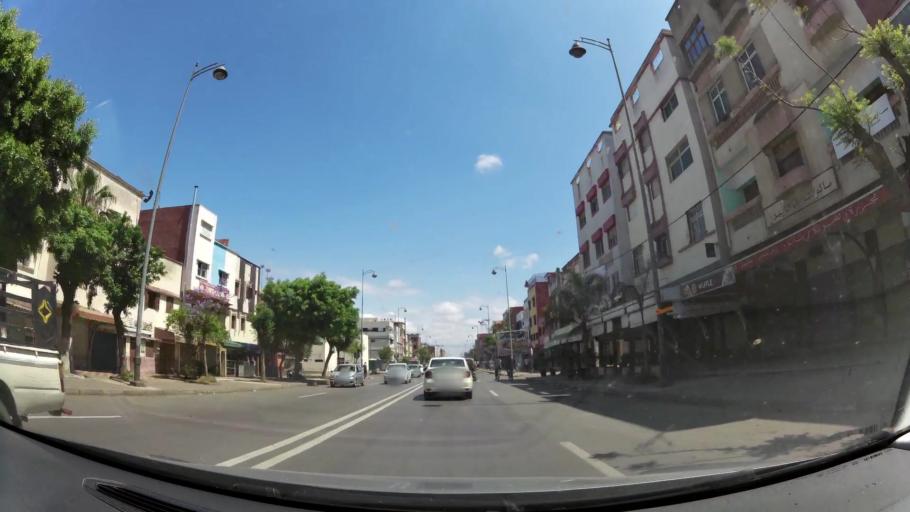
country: MA
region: Gharb-Chrarda-Beni Hssen
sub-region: Kenitra Province
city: Kenitra
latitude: 34.2476
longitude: -6.5540
